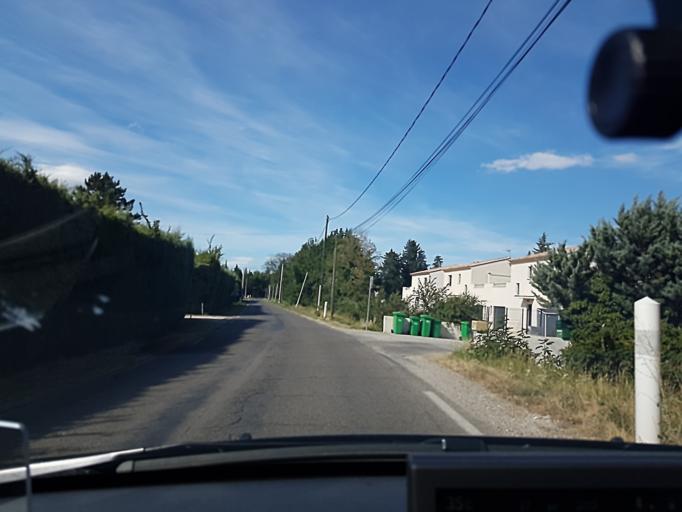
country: FR
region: Provence-Alpes-Cote d'Azur
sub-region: Departement du Vaucluse
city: Caumont-sur-Durance
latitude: 43.9019
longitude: 4.9570
